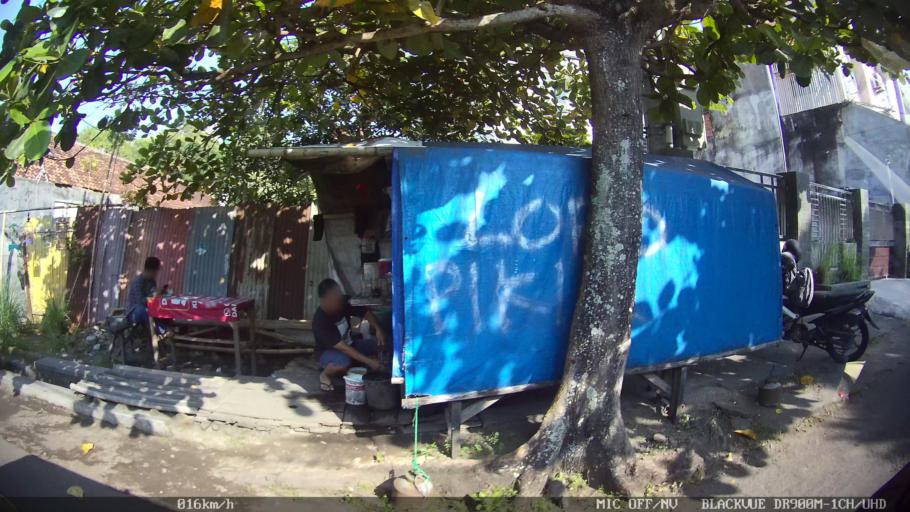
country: ID
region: Daerah Istimewa Yogyakarta
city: Depok
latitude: -7.7590
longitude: 110.4006
